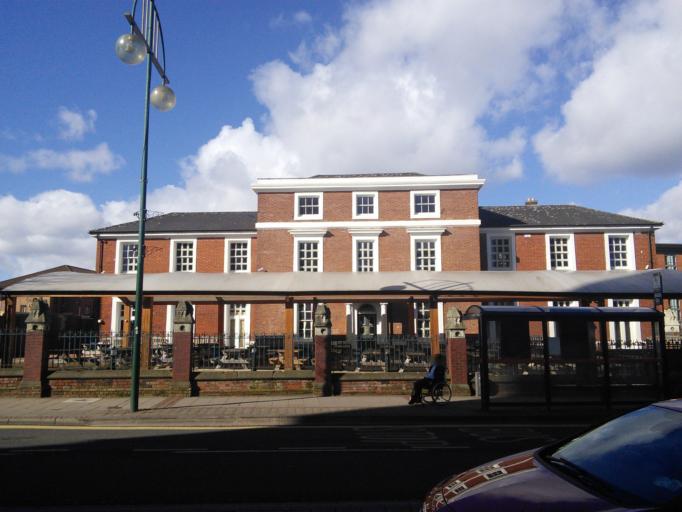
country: GB
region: England
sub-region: City and Borough of Birmingham
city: Birmingham
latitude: 52.4754
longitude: -1.9139
